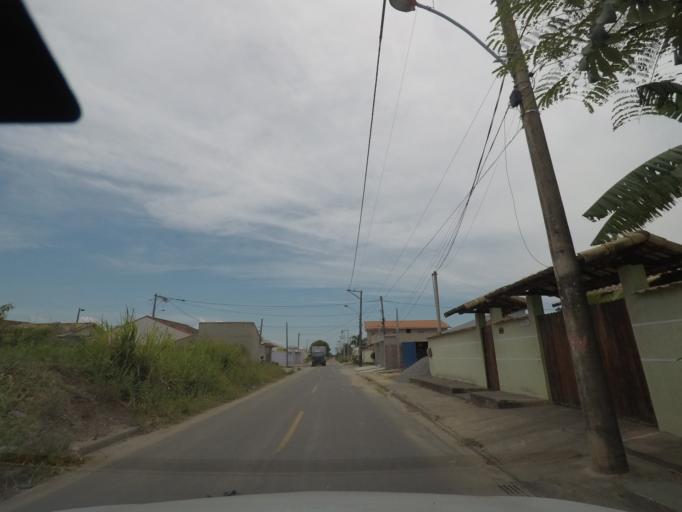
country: BR
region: Rio de Janeiro
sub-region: Marica
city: Marica
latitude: -22.9595
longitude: -42.9582
